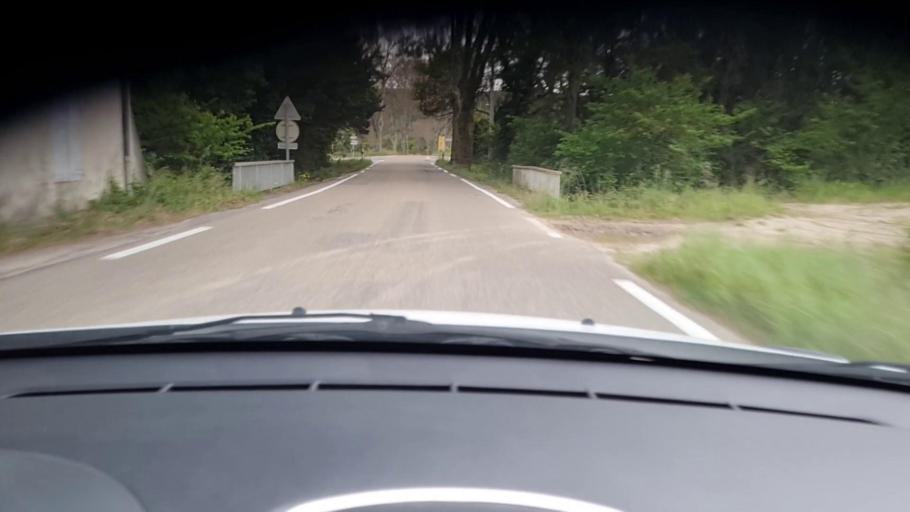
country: FR
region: Languedoc-Roussillon
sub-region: Departement du Gard
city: Blauzac
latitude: 43.9492
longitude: 4.3790
